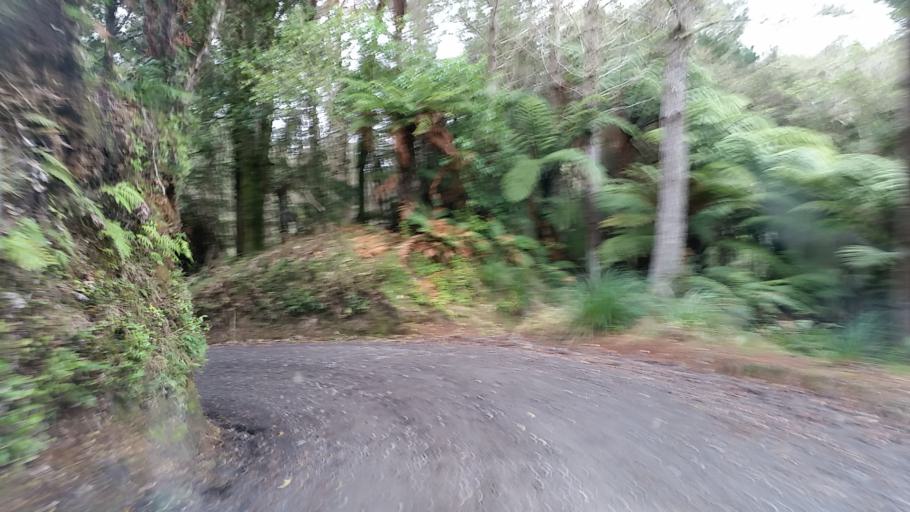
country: NZ
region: Taranaki
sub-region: New Plymouth District
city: Waitara
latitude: -39.1606
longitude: 174.5518
